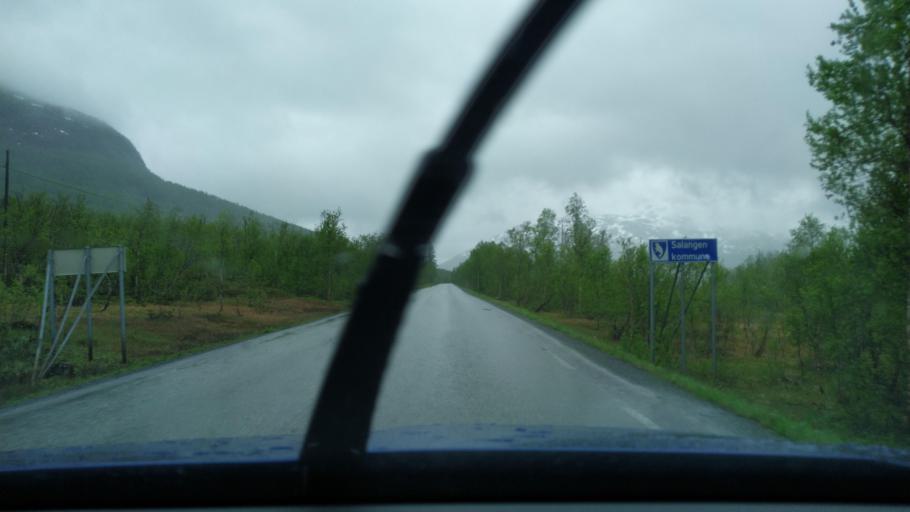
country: NO
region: Troms
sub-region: Dyroy
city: Brostadbotn
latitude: 69.0070
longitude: 17.7268
